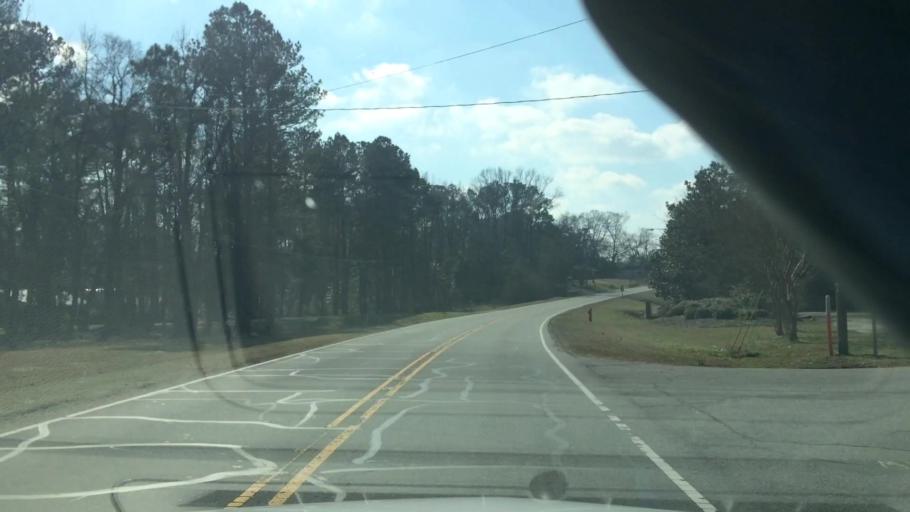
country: US
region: North Carolina
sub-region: Duplin County
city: Beulaville
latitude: 35.0596
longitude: -77.7411
